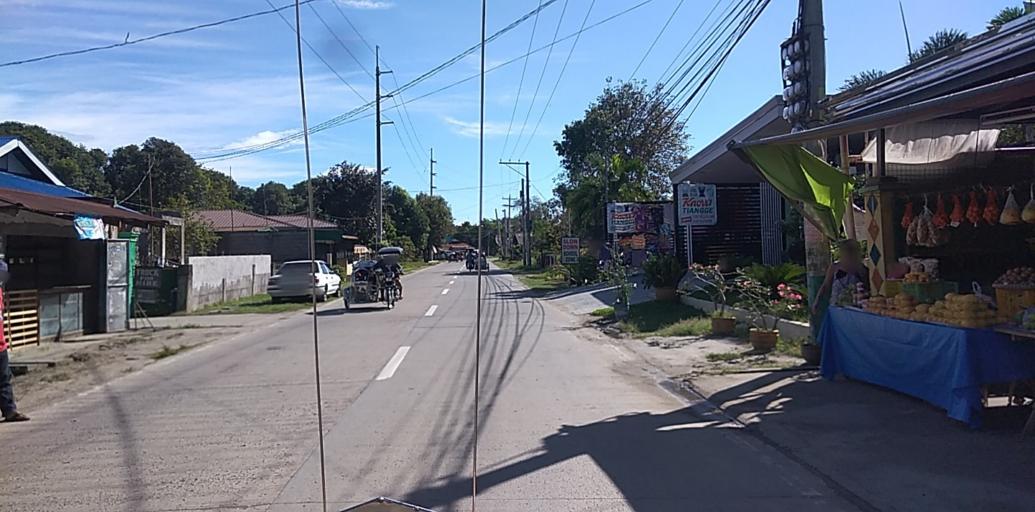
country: PH
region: Central Luzon
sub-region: Province of Pampanga
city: Santo Domingo
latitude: 15.0723
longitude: 120.7603
